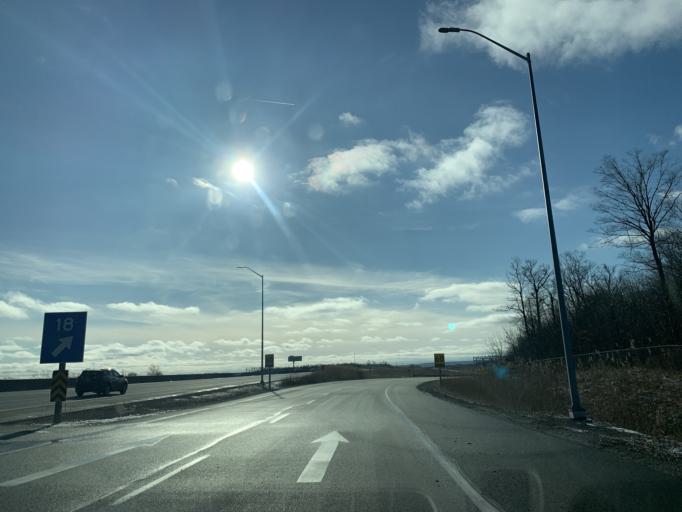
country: CA
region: Ontario
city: Oakville
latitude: 43.4880
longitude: -79.7623
